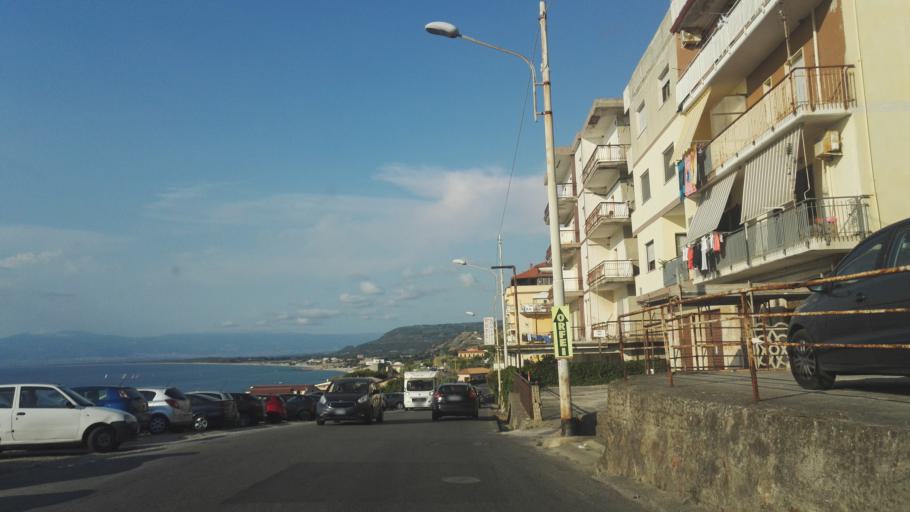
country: IT
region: Calabria
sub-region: Provincia di Vibo-Valentia
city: Pizzo
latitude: 38.7413
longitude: 16.1749
